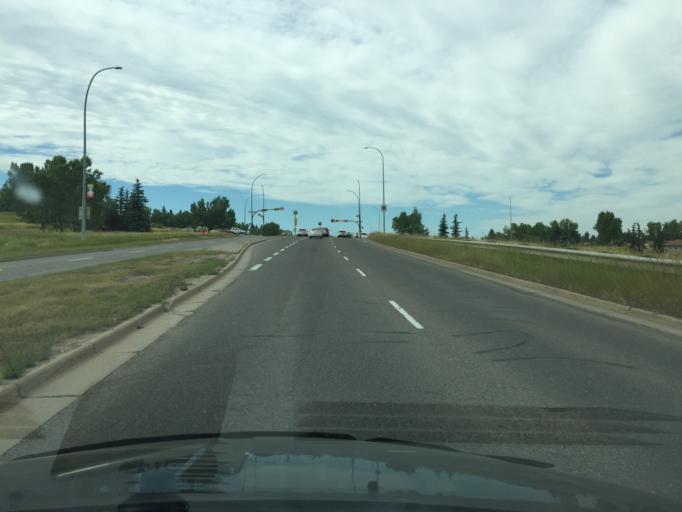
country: CA
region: Alberta
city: Calgary
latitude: 50.9297
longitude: -114.0317
